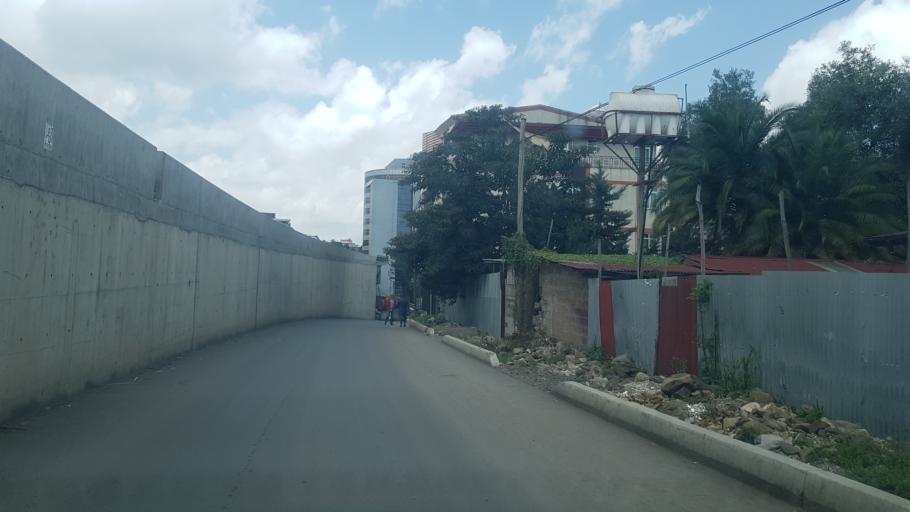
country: ET
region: Adis Abeba
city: Addis Ababa
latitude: 8.9957
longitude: 38.7573
